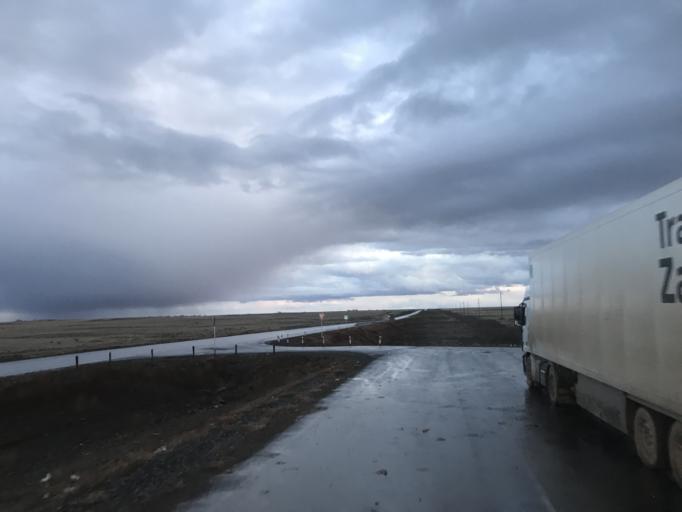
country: KZ
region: Qostanay
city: Ordzhonikidze
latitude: 52.4476
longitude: 61.7720
